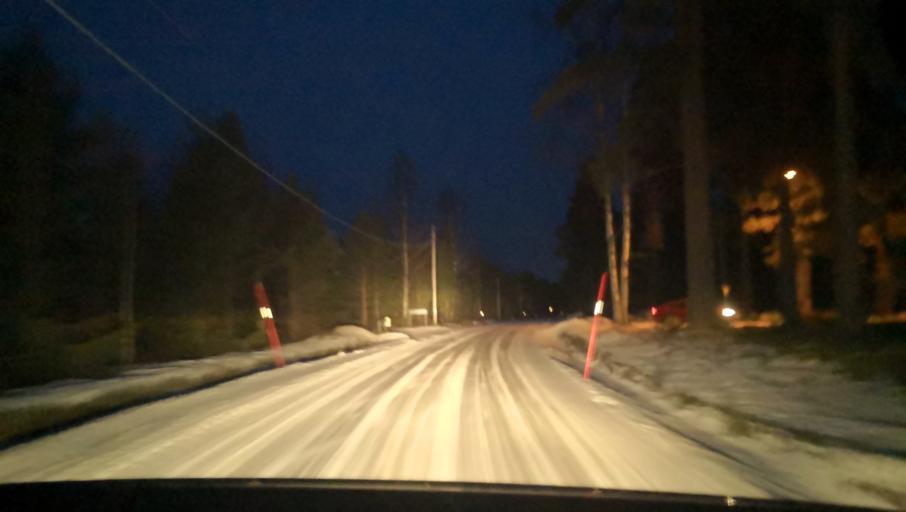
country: SE
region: Uppsala
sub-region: Heby Kommun
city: Tarnsjo
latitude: 60.2689
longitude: 16.7930
